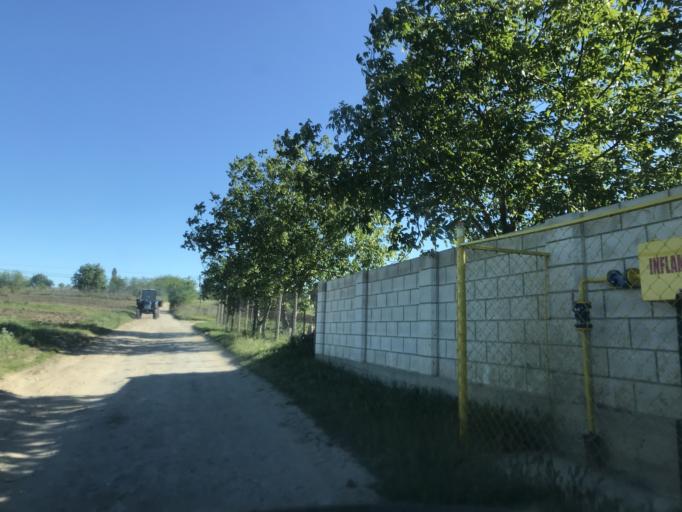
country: MD
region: Chisinau
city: Cricova
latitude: 47.2372
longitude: 28.8154
